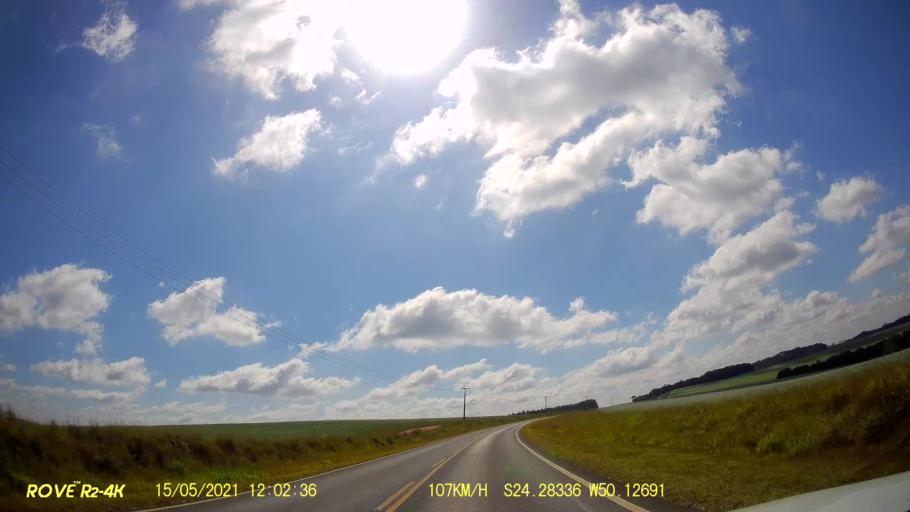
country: BR
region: Parana
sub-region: Pirai Do Sul
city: Pirai do Sul
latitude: -24.2834
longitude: -50.1266
